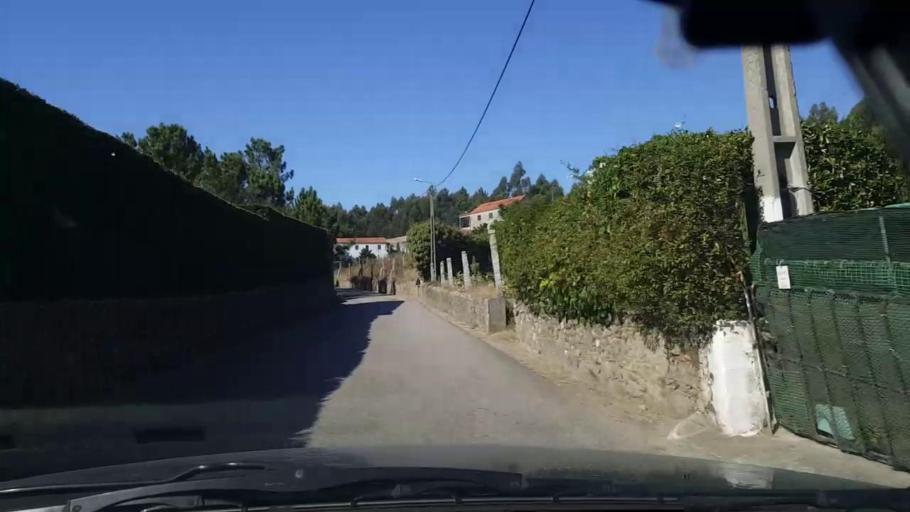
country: PT
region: Porto
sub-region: Vila do Conde
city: Arvore
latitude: 41.3641
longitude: -8.6458
